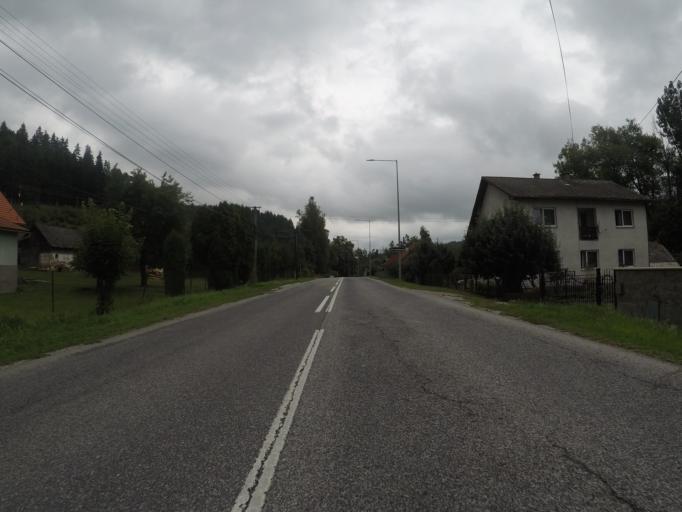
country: SK
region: Kosicky
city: Spisska Nova Ves
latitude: 48.9059
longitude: 20.5221
